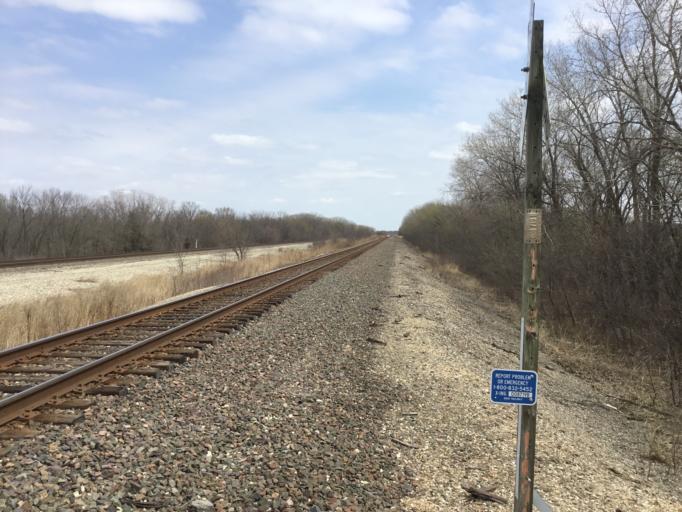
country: US
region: Kansas
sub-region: Lyon County
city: Emporia
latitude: 38.4053
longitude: -96.3274
